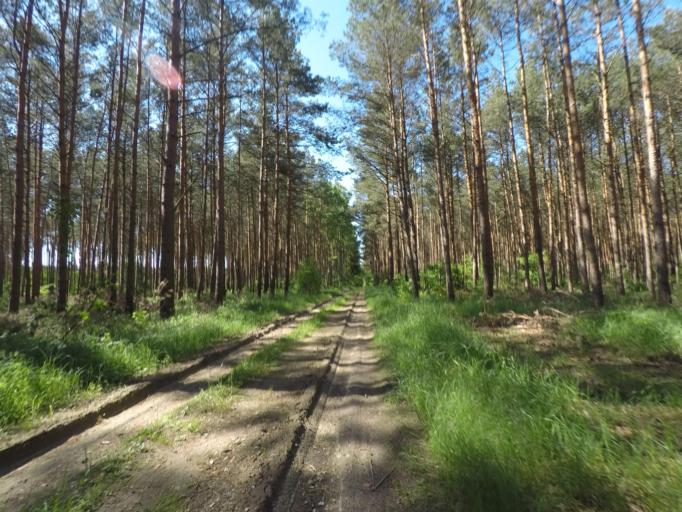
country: DE
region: Brandenburg
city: Melchow
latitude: 52.8219
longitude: 13.7522
